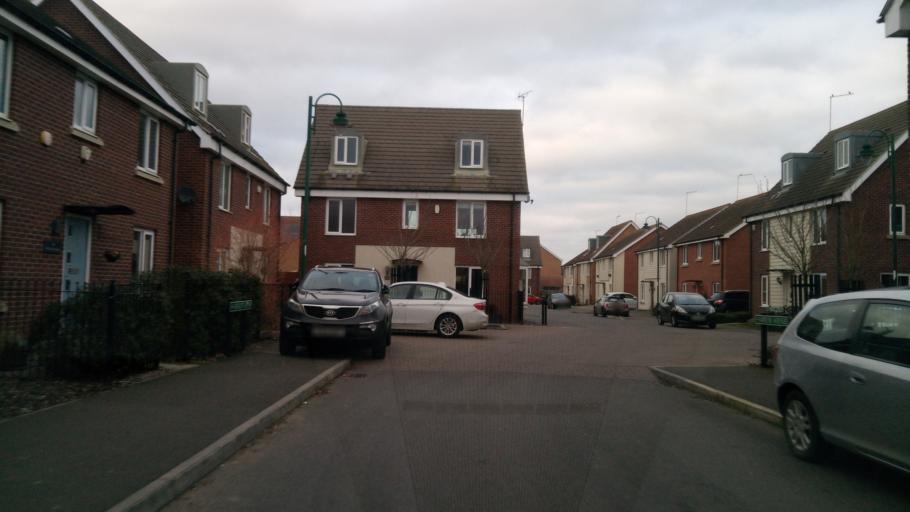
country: GB
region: England
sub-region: Cambridgeshire
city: Yaxley
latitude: 52.5315
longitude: -0.2834
